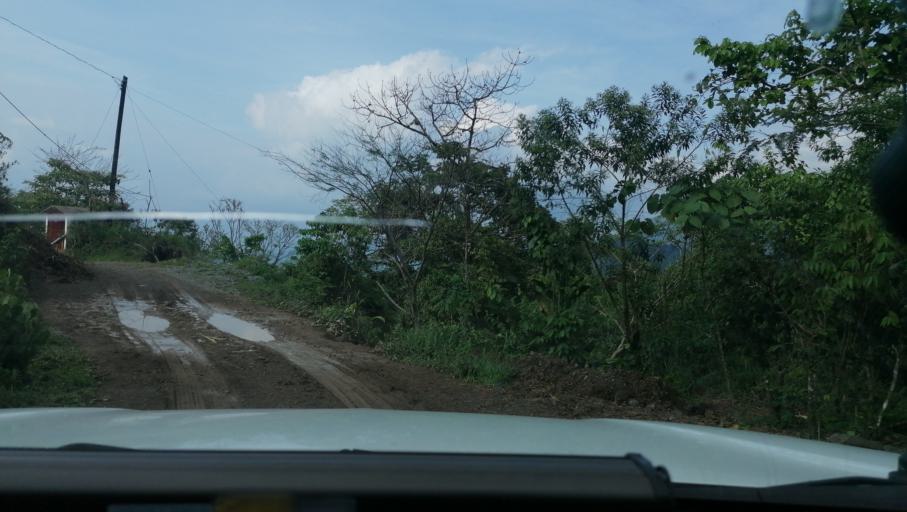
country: MX
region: Chiapas
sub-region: Tapilula
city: San Francisco Jacona
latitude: 17.3115
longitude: -93.1010
